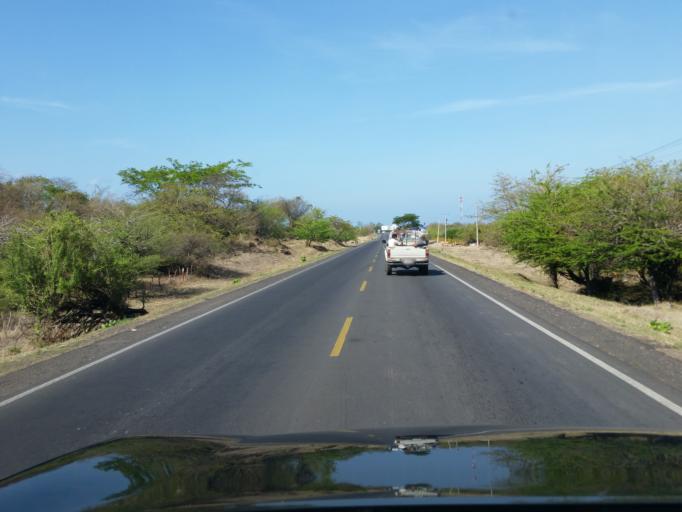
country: NI
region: Leon
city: La Paz Centro
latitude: 12.2735
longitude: -86.7312
